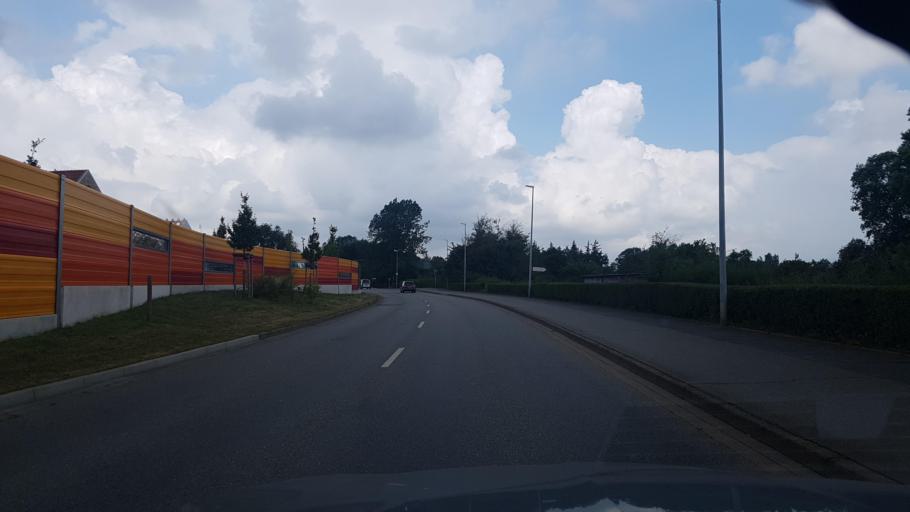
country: DE
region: Schleswig-Holstein
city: Husum
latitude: 54.4934
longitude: 9.0327
